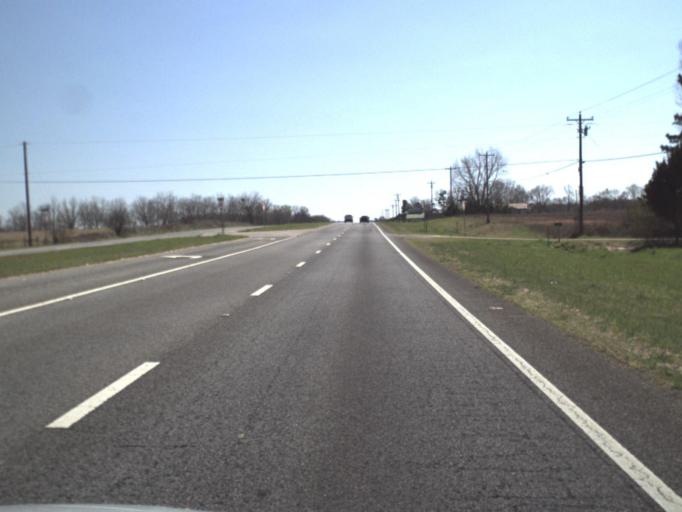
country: US
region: Florida
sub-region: Jackson County
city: Graceville
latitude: 30.9317
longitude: -85.3879
